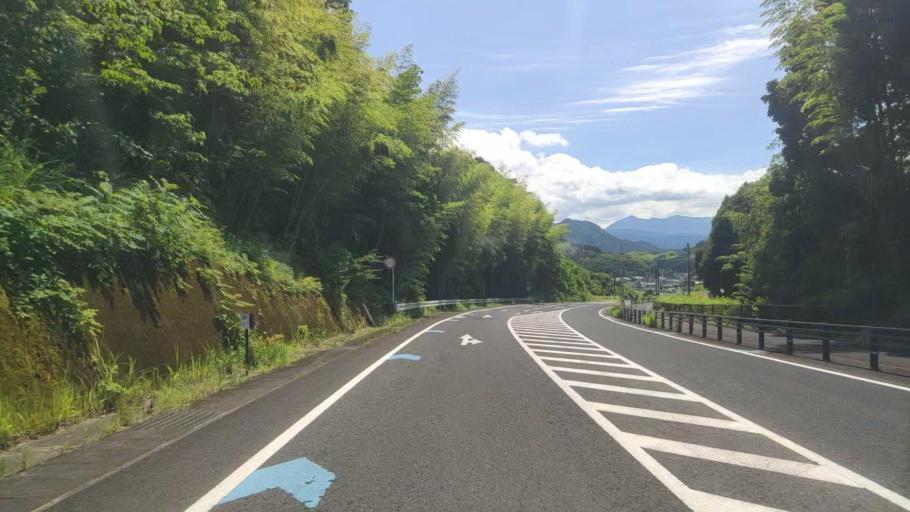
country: JP
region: Wakayama
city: Shingu
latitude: 33.7428
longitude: 136.0074
